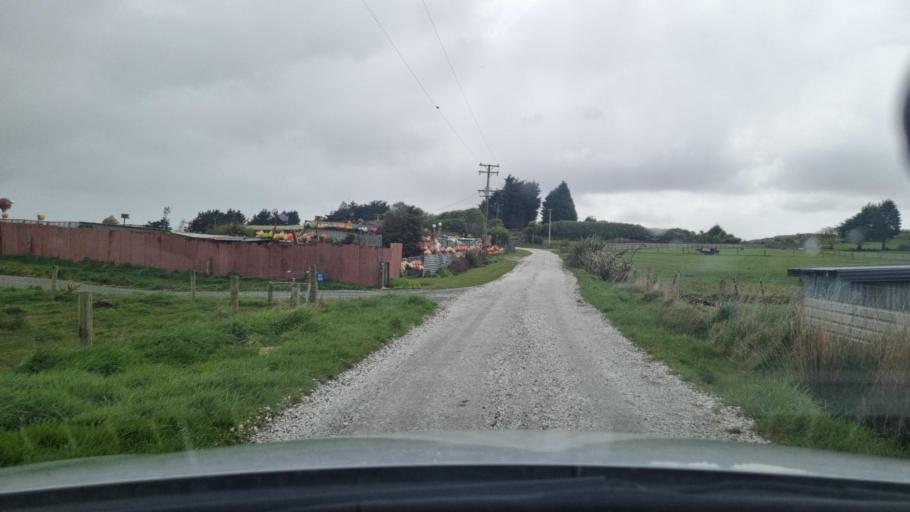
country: NZ
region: Southland
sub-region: Invercargill City
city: Bluff
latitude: -46.5400
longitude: 168.2905
